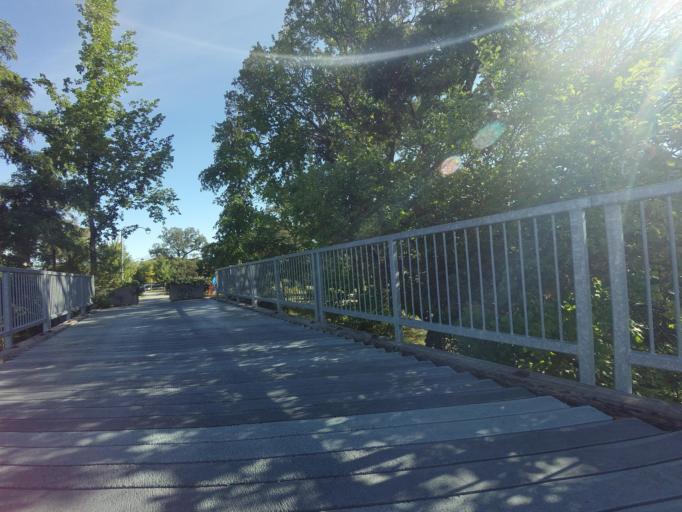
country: CA
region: Ontario
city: Omemee
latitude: 44.5374
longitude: -78.7416
